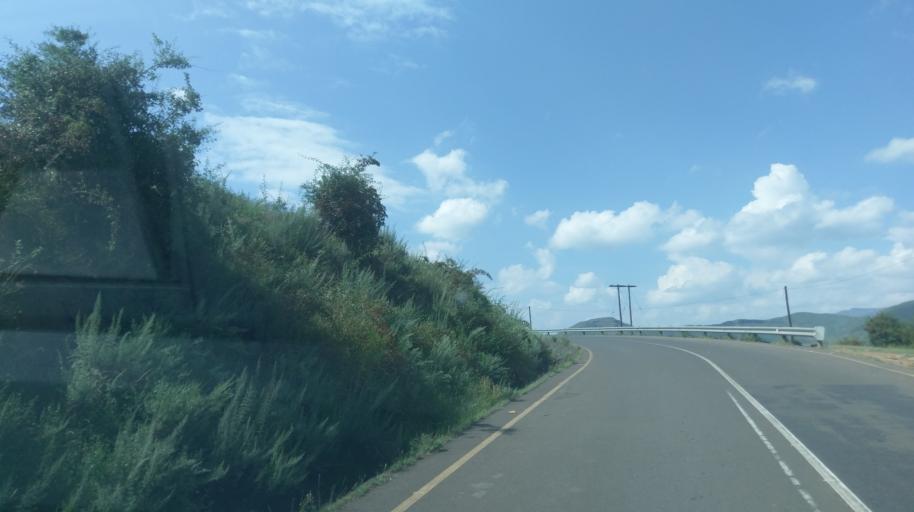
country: LS
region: Thaba-Tseka
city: Thaba-Tseka
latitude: -29.1213
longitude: 28.4928
